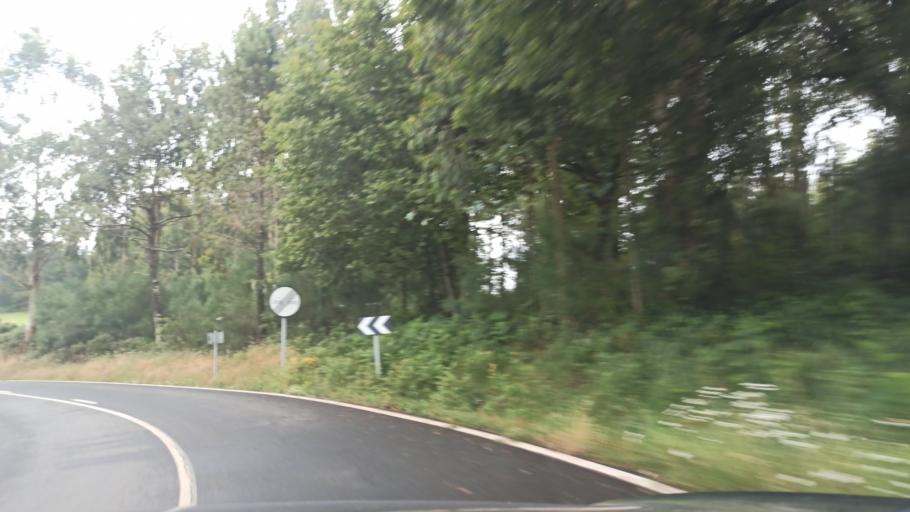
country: ES
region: Galicia
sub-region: Provincia da Coruna
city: Santiso
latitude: 42.7853
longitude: -8.0716
